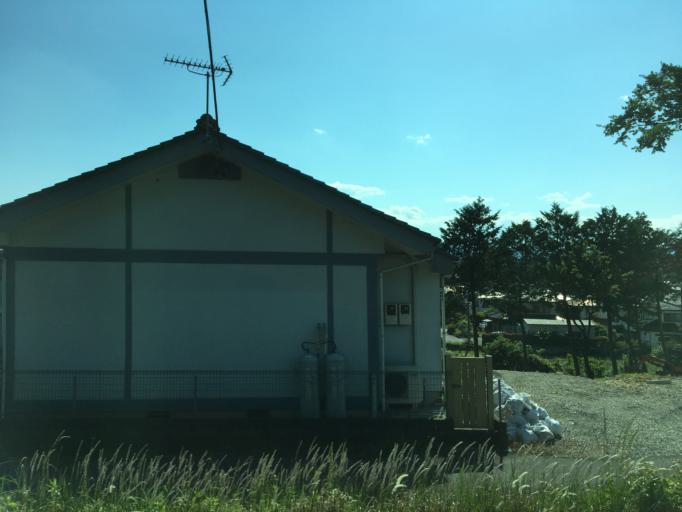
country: JP
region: Saitama
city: Morohongo
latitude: 35.9726
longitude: 139.3394
